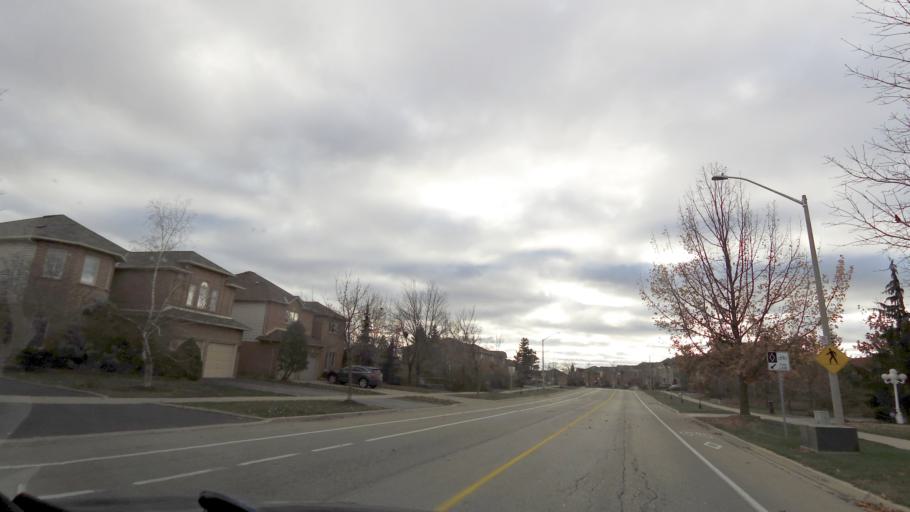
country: CA
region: Ontario
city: Oakville
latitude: 43.4706
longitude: -79.7351
